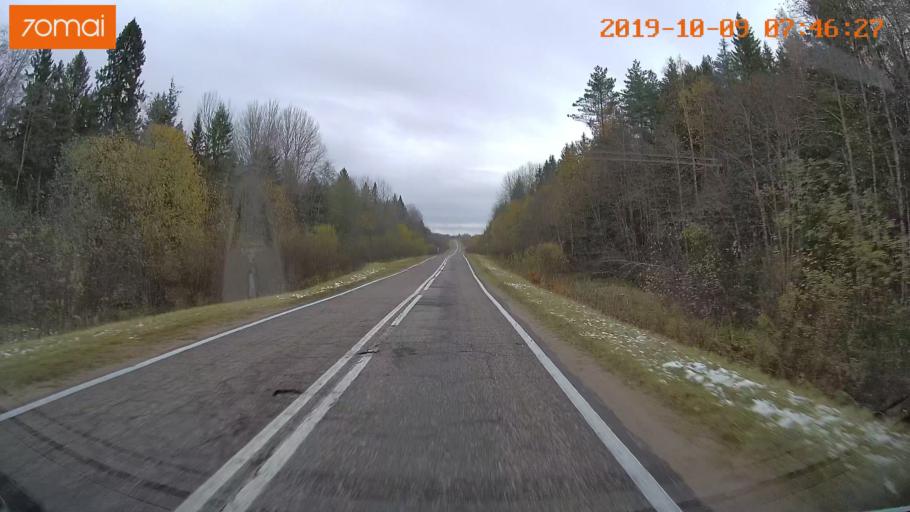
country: RU
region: Jaroslavl
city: Kukoboy
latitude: 58.6561
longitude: 39.7880
